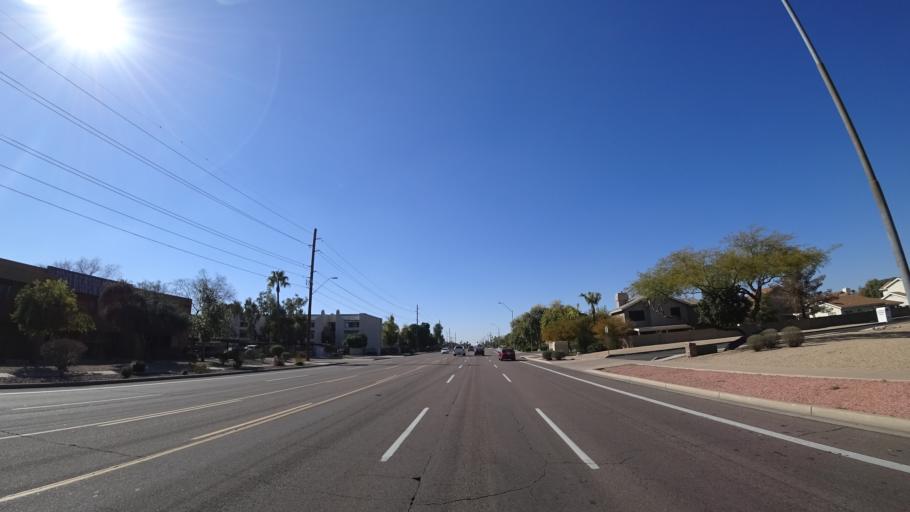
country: US
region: Arizona
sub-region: Maricopa County
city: Peoria
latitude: 33.6547
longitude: -112.1482
